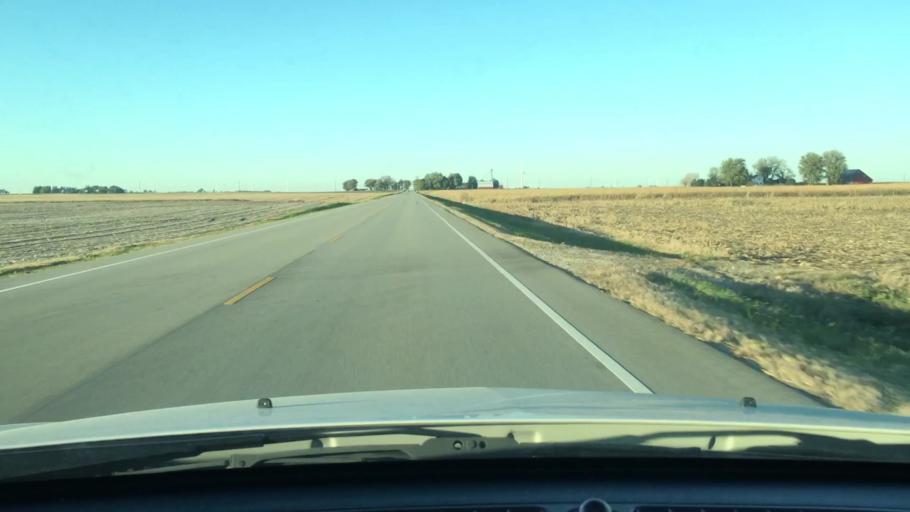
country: US
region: Illinois
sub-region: DeKalb County
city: Waterman
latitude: 41.8107
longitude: -88.8864
